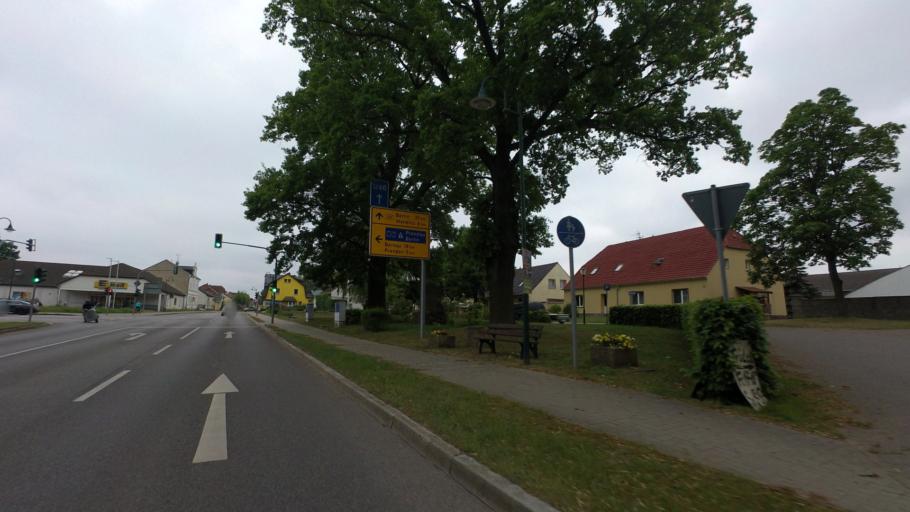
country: DE
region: Brandenburg
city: Wandlitz
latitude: 52.7914
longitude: 13.4801
